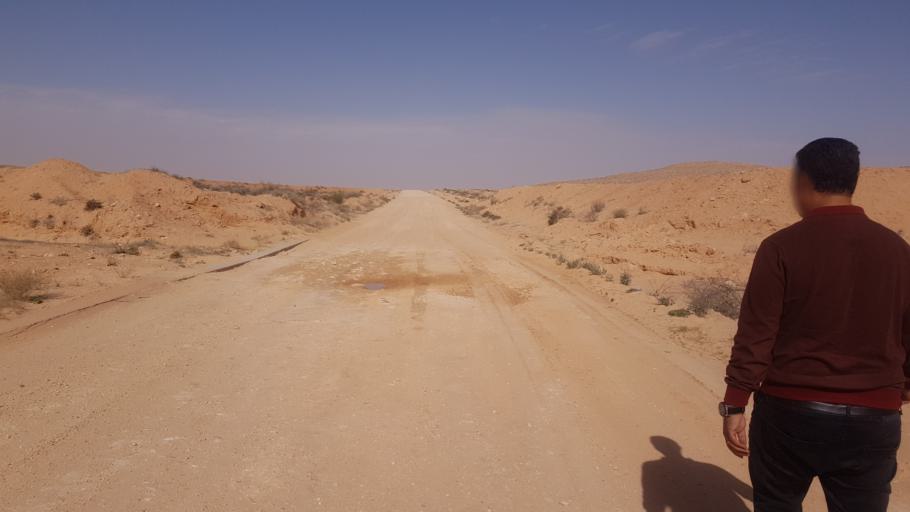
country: TN
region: Qabis
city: El Hamma
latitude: 33.6544
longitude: 9.7358
